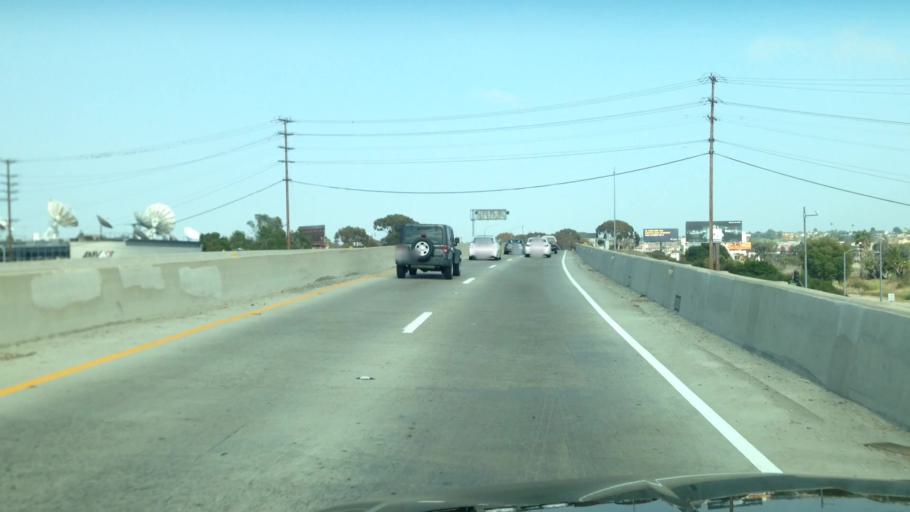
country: US
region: California
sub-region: Los Angeles County
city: Marina del Rey
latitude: 33.9817
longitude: -118.4296
